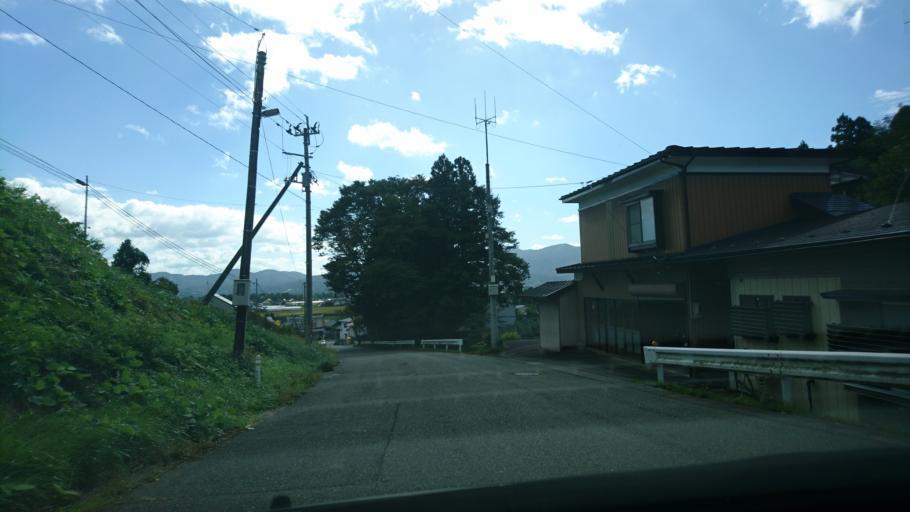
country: JP
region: Iwate
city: Mizusawa
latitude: 39.0694
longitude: 141.1269
